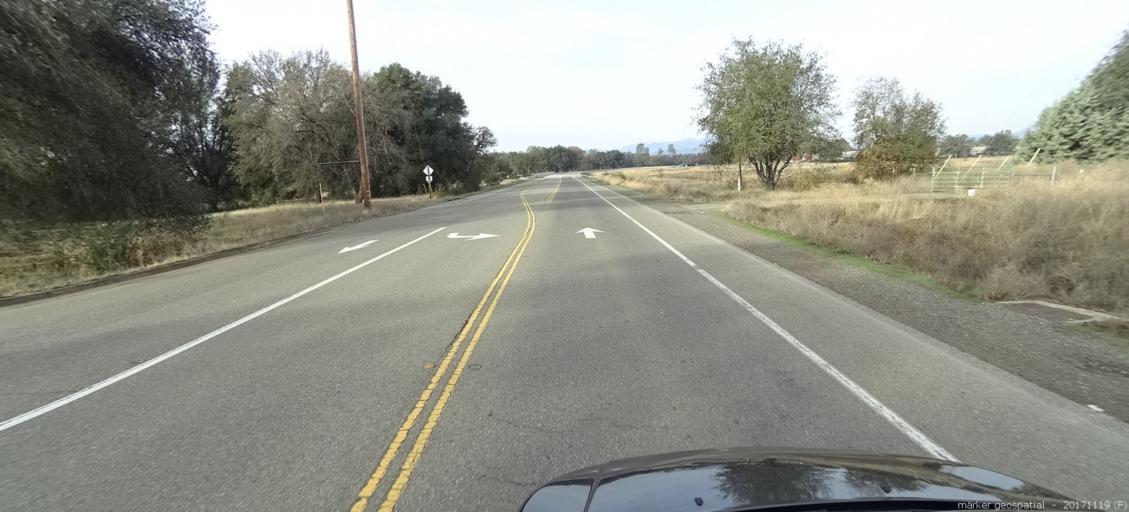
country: US
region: California
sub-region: Shasta County
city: Anderson
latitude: 40.5056
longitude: -122.3057
